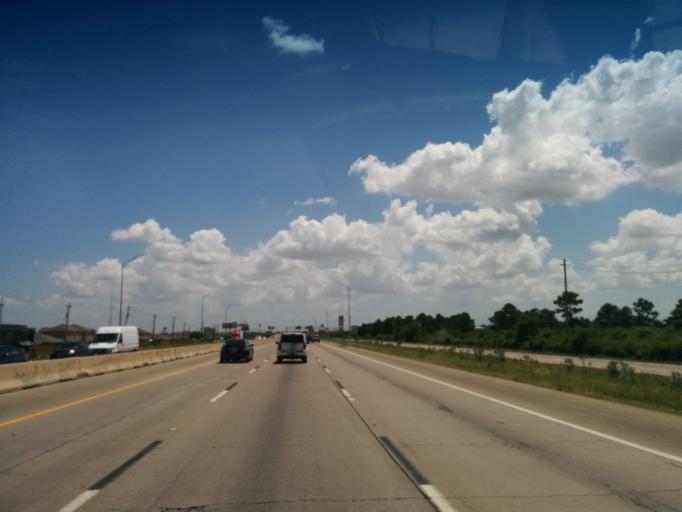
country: US
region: Texas
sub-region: Harris County
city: Highlands
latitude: 29.7942
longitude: -95.0406
